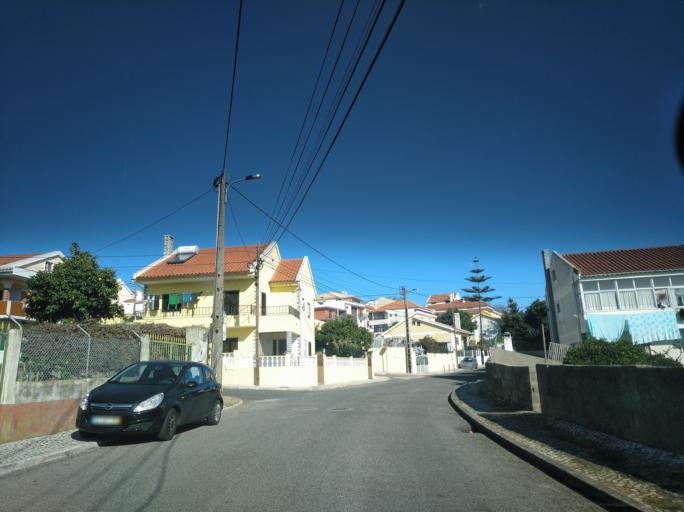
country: PT
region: Lisbon
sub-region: Odivelas
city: Famoes
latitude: 38.7989
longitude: -9.2189
